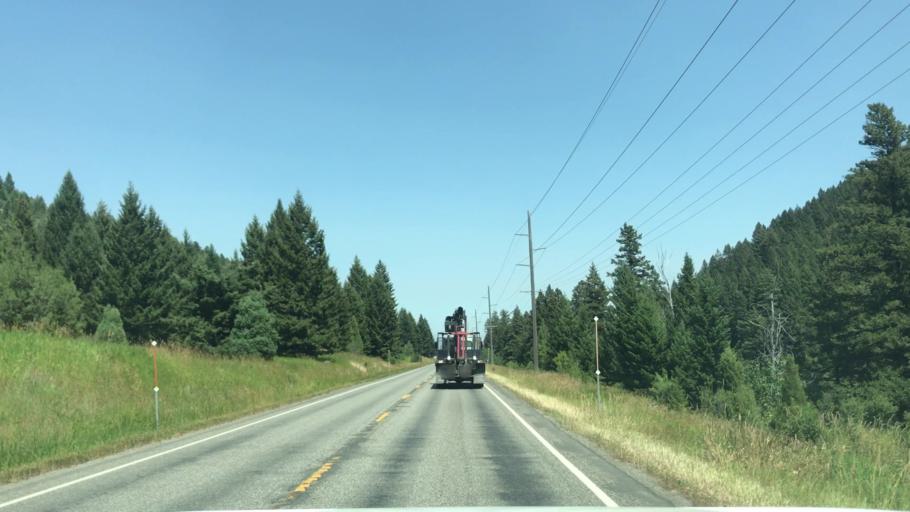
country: US
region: Montana
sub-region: Gallatin County
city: Four Corners
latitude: 45.5130
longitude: -111.2579
